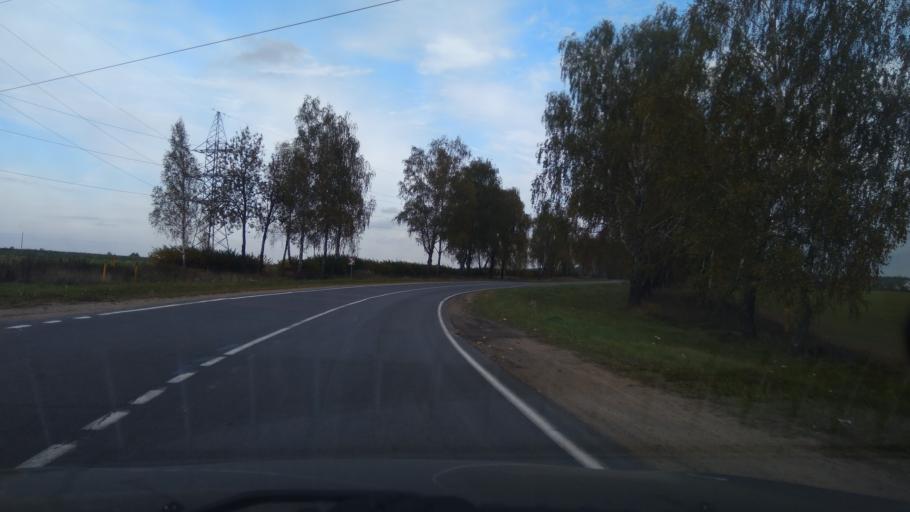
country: BY
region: Minsk
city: Rudzyensk
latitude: 53.6184
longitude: 27.8546
